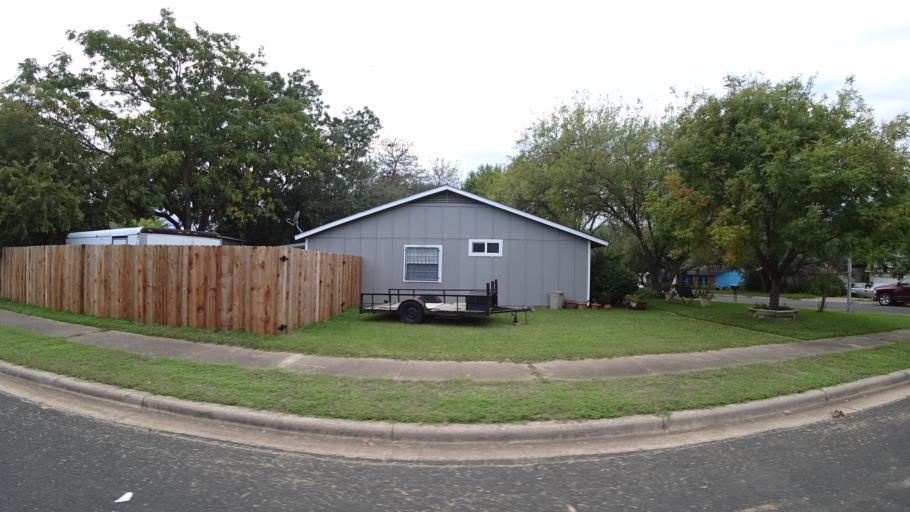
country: US
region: Texas
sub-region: Travis County
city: Onion Creek
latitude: 30.2011
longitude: -97.7814
